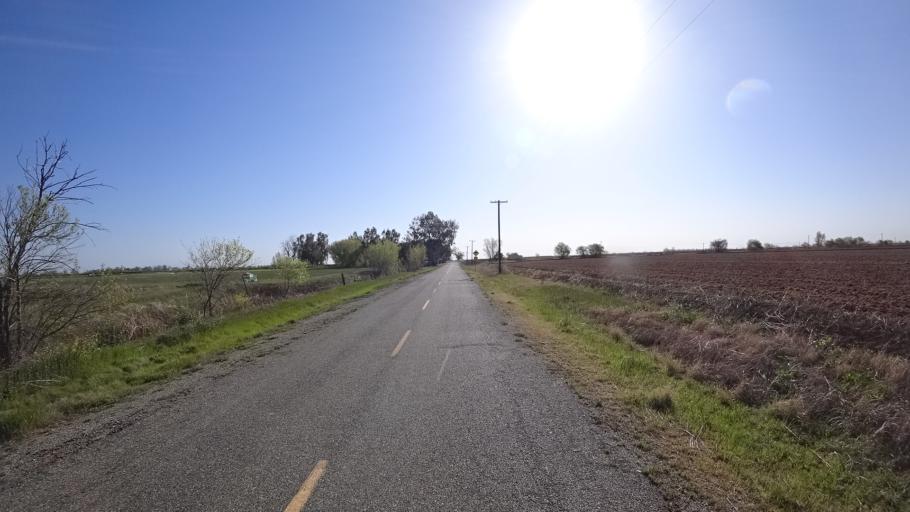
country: US
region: California
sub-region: Glenn County
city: Willows
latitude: 39.5096
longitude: -122.1773
